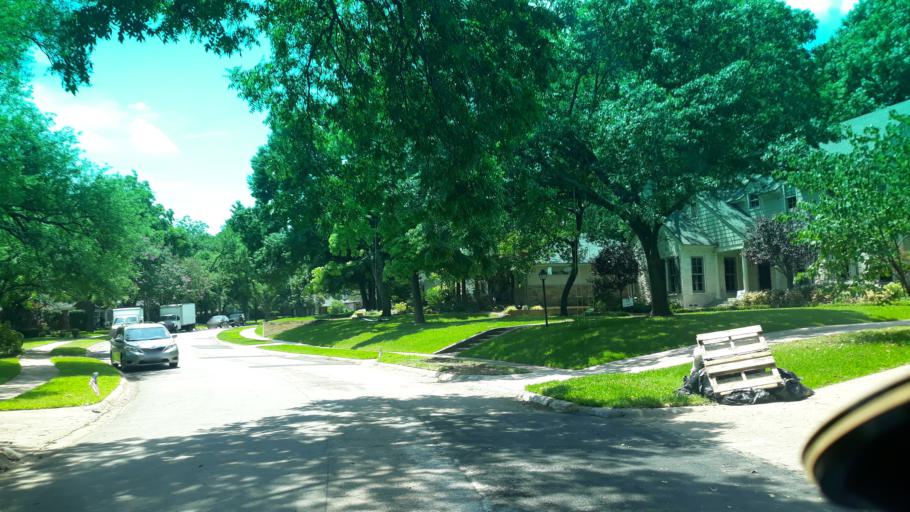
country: US
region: Texas
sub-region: Dallas County
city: Highland Park
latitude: 32.8250
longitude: -96.7356
